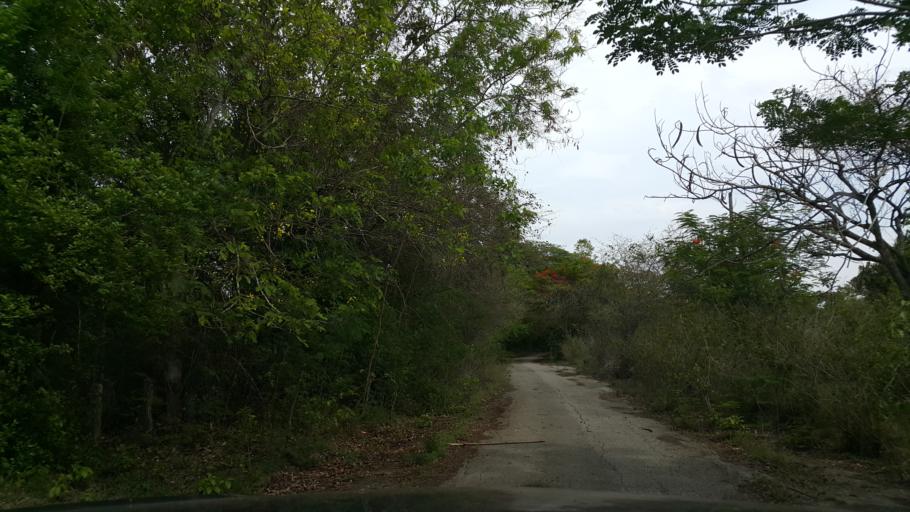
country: TH
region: Chiang Mai
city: San Kamphaeng
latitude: 18.7578
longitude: 99.1186
